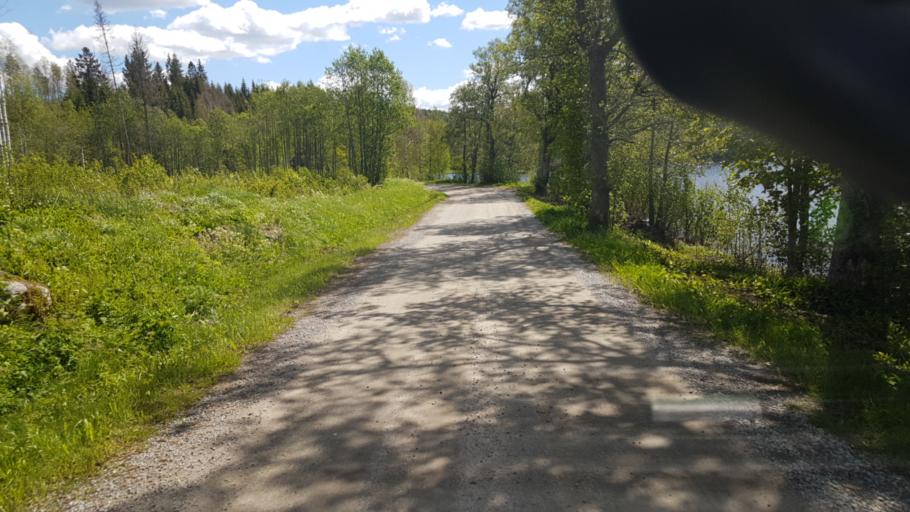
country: SE
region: Vaermland
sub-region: Arvika Kommun
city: Arvika
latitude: 59.7111
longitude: 12.8513
